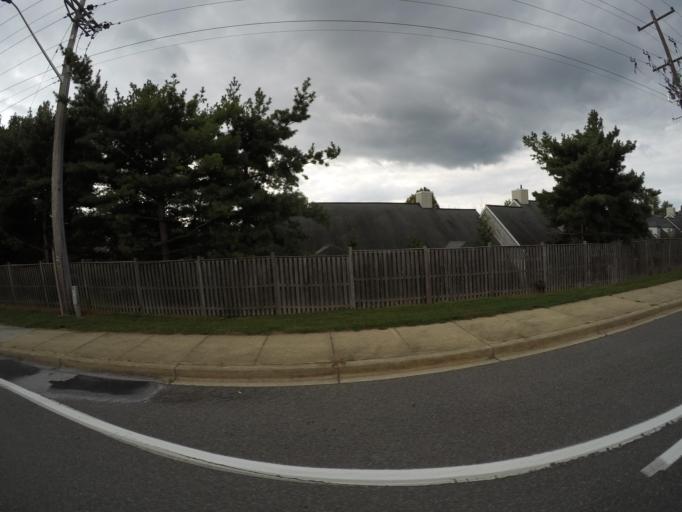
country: US
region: Delaware
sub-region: New Castle County
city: Brookside
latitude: 39.6756
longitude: -75.7288
